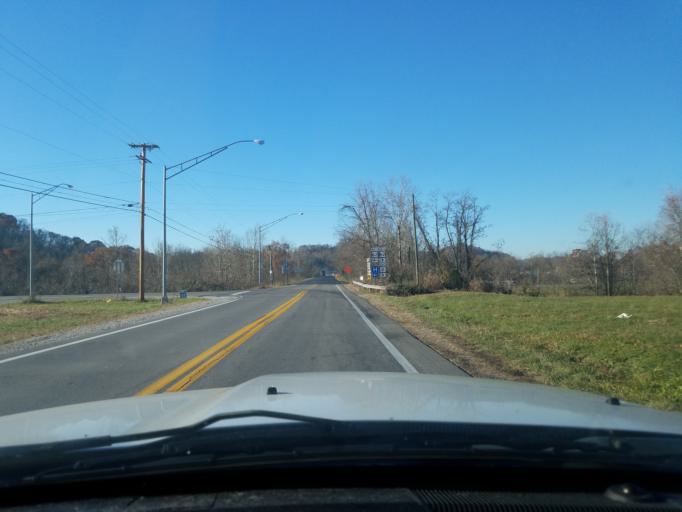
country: US
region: West Virginia
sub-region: Jackson County
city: Ravenswood
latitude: 38.8885
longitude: -81.8404
